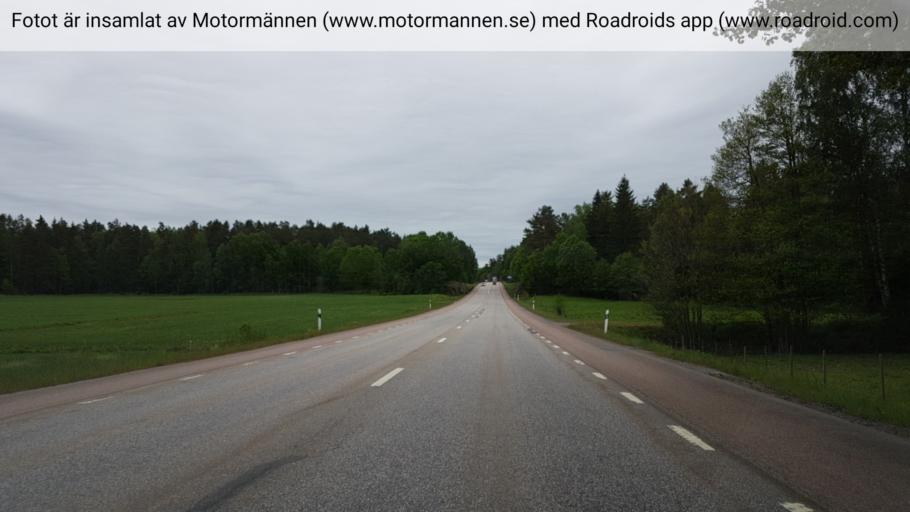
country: SE
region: Kalmar
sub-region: Vasterviks Kommun
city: Ankarsrum
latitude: 57.6737
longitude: 16.4430
